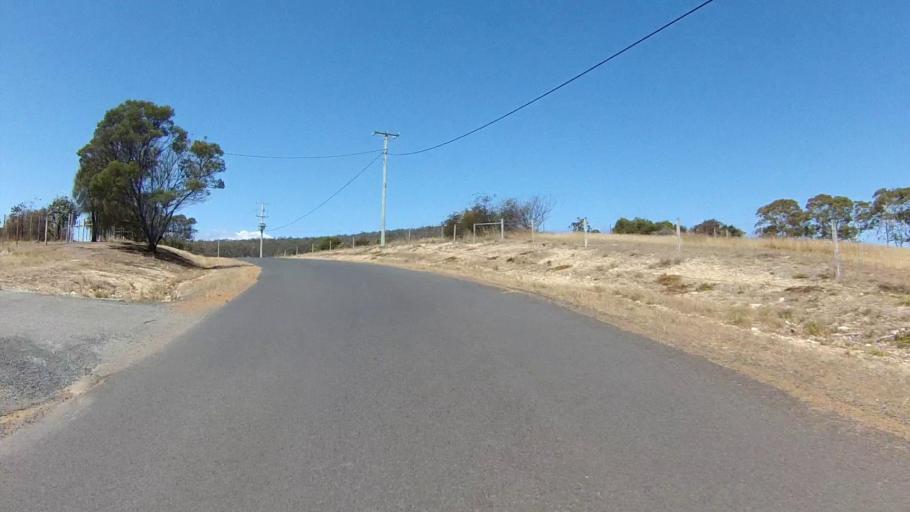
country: AU
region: Tasmania
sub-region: Clarence
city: Sandford
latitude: -42.9568
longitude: 147.4783
